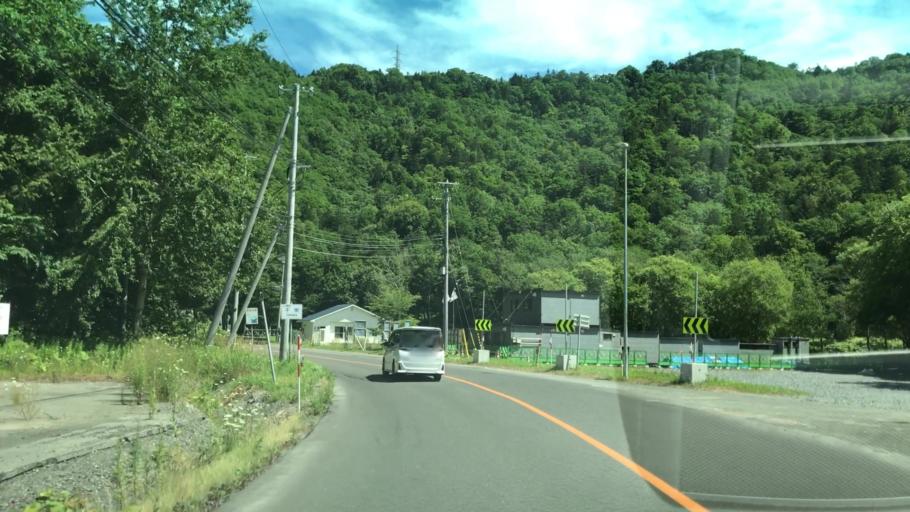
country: JP
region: Hokkaido
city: Shimo-furano
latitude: 42.9120
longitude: 142.5862
